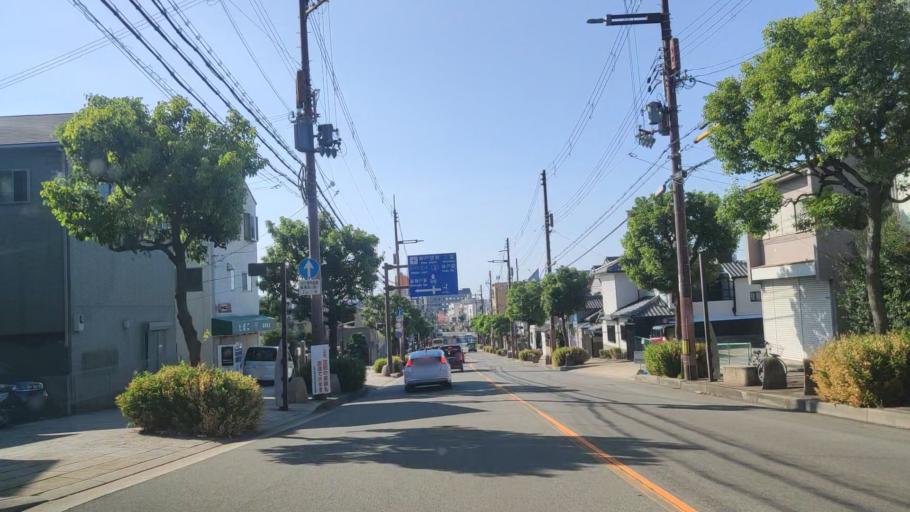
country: JP
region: Hyogo
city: Kobe
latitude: 34.6923
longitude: 135.1671
